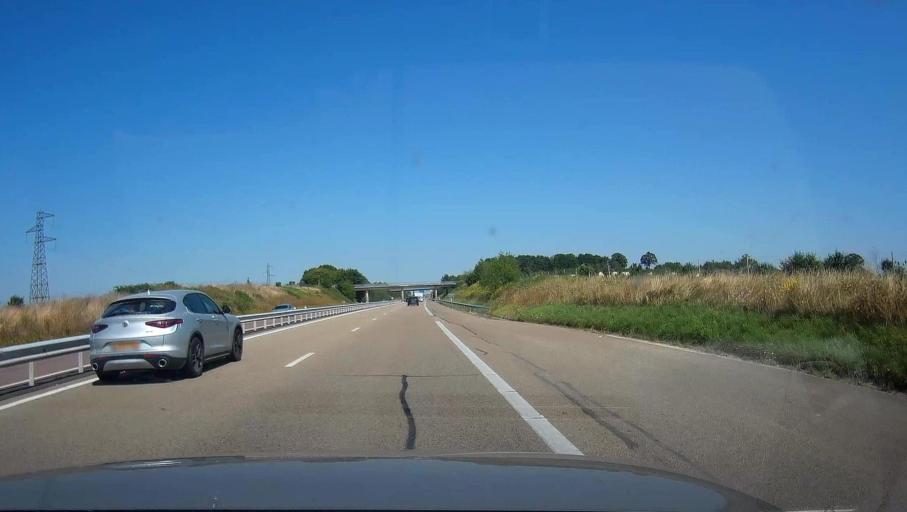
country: FR
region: Champagne-Ardenne
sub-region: Departement de l'Aube
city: Saint-Parres-aux-Tertres
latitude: 48.2821
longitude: 4.1642
